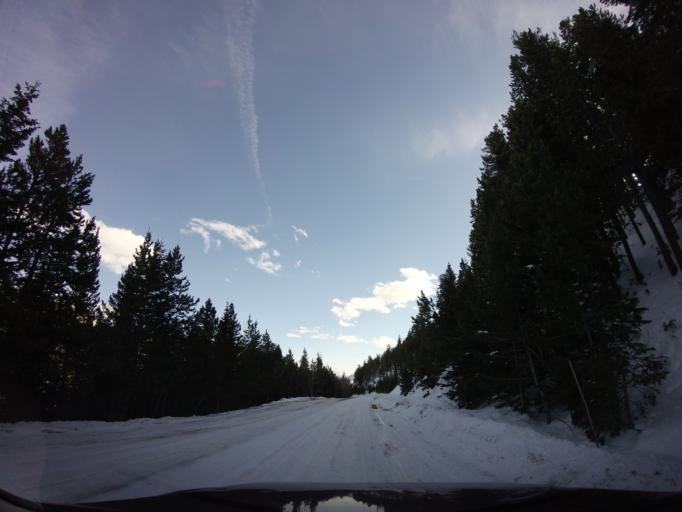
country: US
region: Montana
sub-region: Carbon County
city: Red Lodge
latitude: 45.1828
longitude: -109.3250
